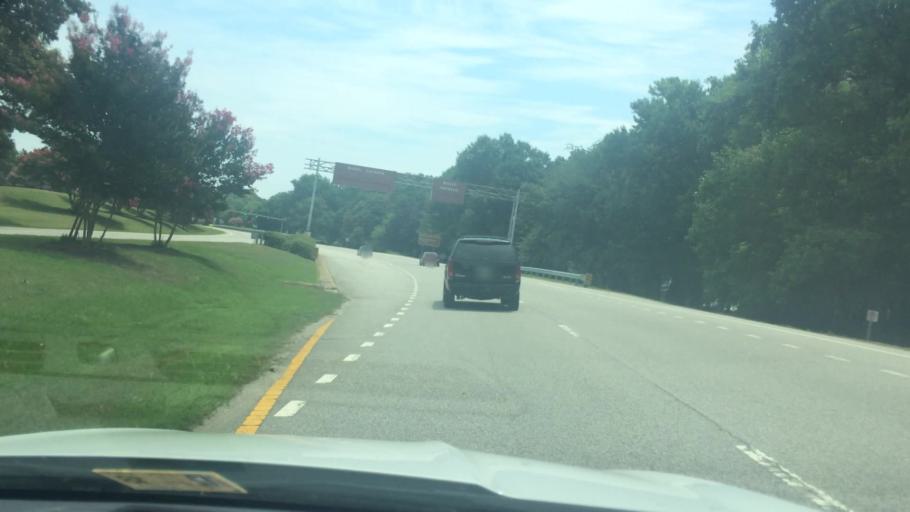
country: US
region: Virginia
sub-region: City of Williamsburg
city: Williamsburg
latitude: 37.2412
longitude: -76.6535
